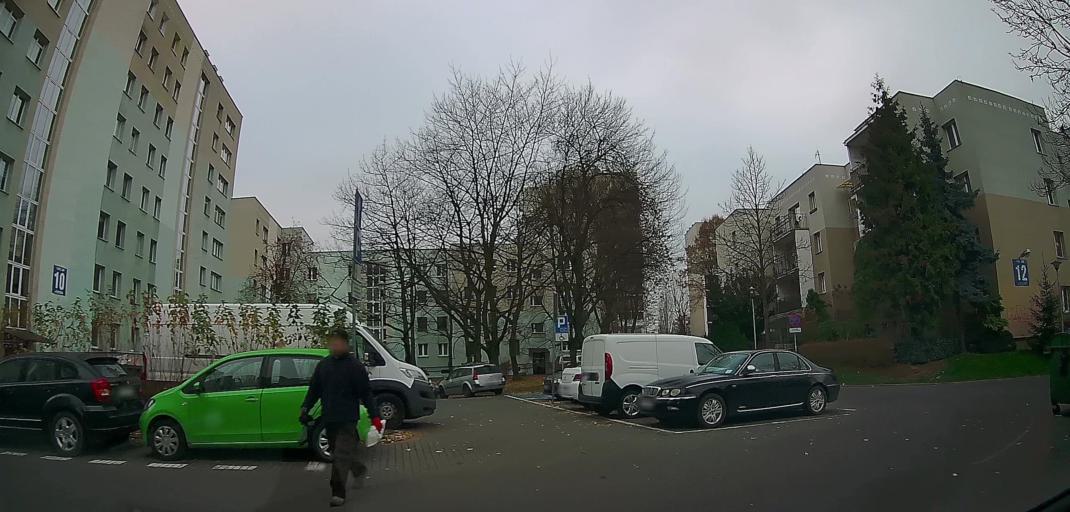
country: PL
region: Masovian Voivodeship
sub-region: Warszawa
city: Ursynow
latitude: 52.1590
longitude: 21.0237
